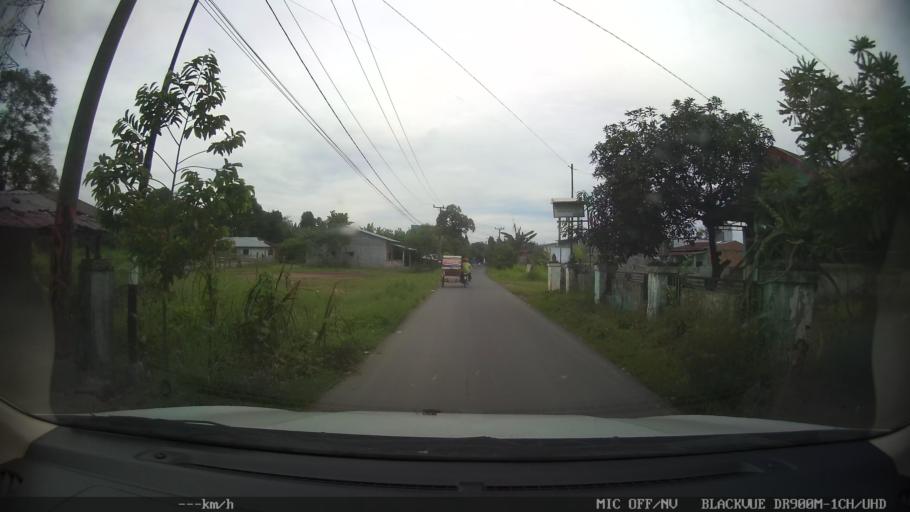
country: ID
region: North Sumatra
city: Sunggal
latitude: 3.6175
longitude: 98.5983
